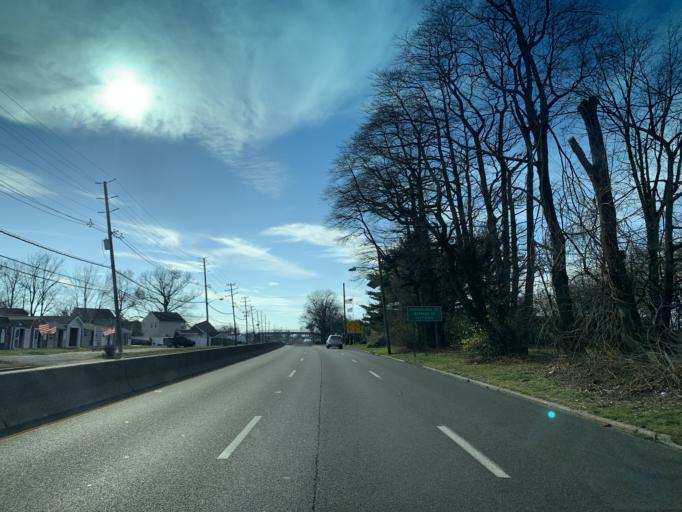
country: US
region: New Jersey
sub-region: Camden County
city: Pennsauken
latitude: 39.9584
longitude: -75.0559
